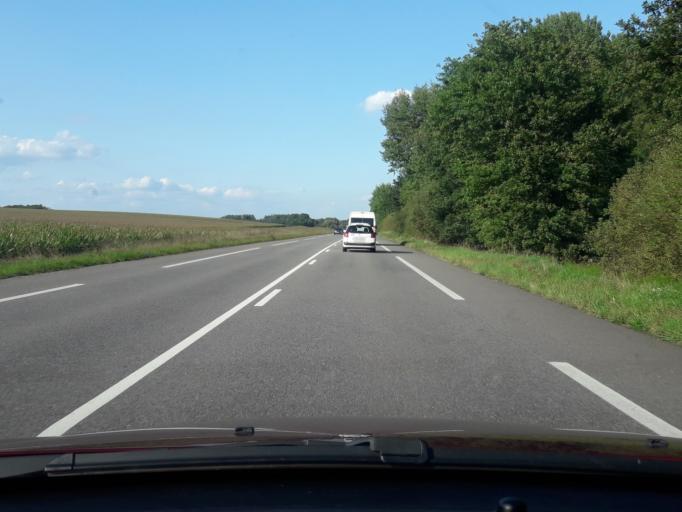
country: FR
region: Alsace
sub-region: Departement du Bas-Rhin
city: Wissembourg
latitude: 48.9705
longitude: 7.9527
